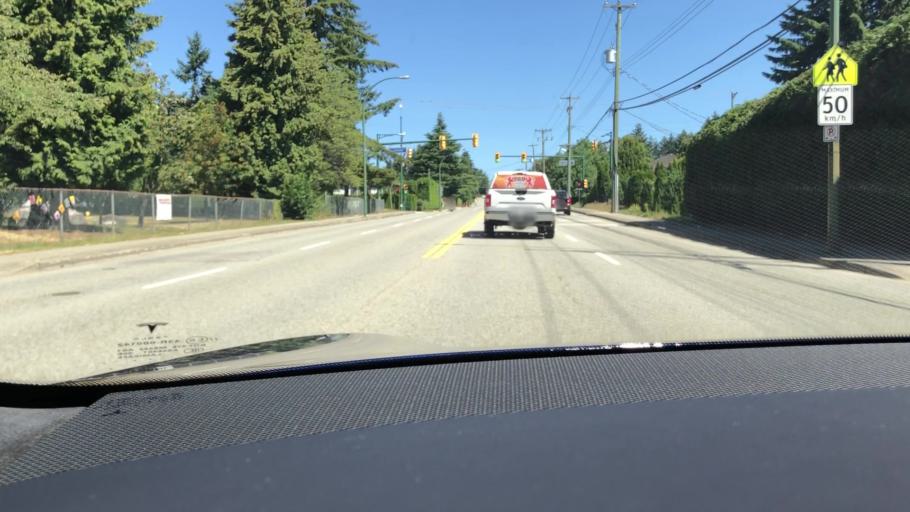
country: CA
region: British Columbia
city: Port Moody
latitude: 49.2389
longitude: -122.8731
